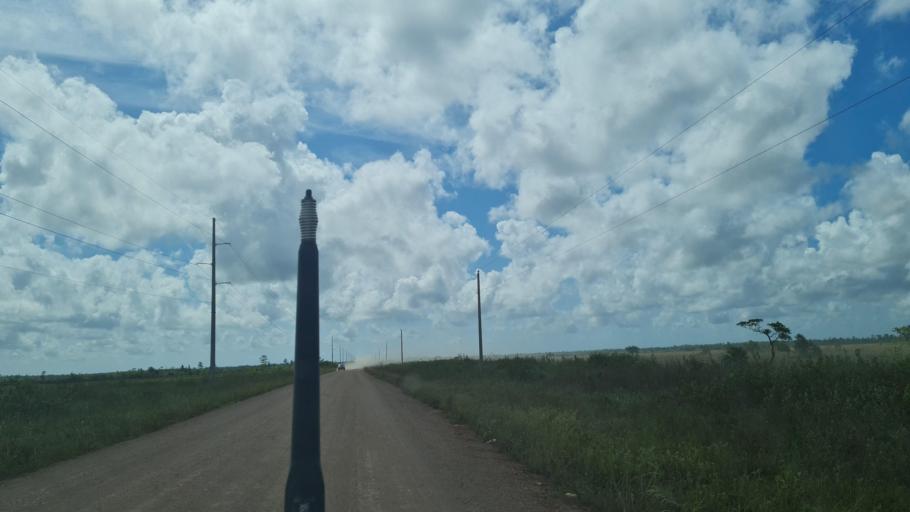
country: NI
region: Atlantico Norte (RAAN)
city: Puerto Cabezas
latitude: 14.1102
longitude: -83.6102
